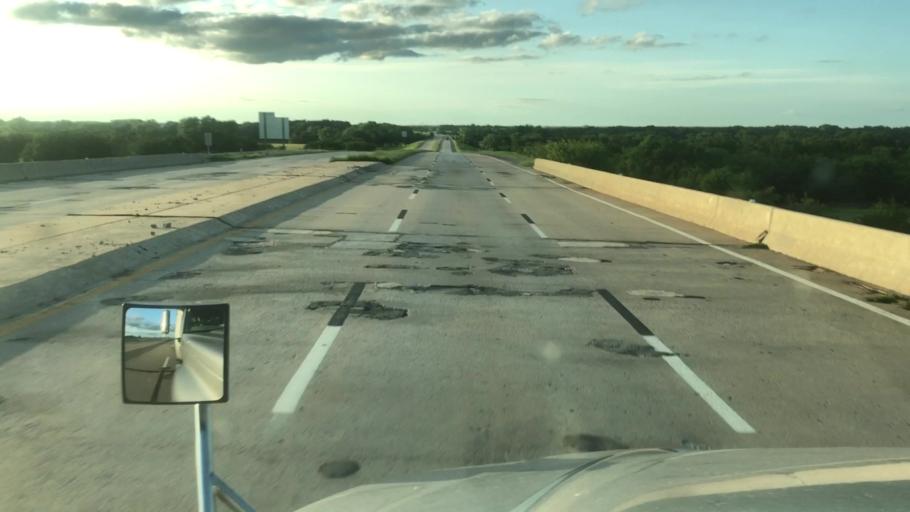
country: US
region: Oklahoma
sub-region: Pawnee County
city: Pawnee
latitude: 36.2978
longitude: -96.9867
